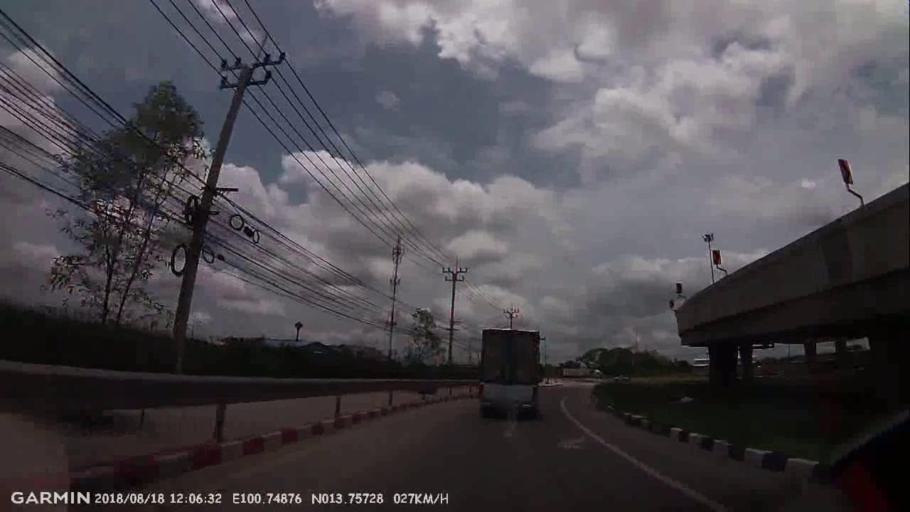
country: TH
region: Bangkok
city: Lat Krabang
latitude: 13.7576
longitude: 100.7504
